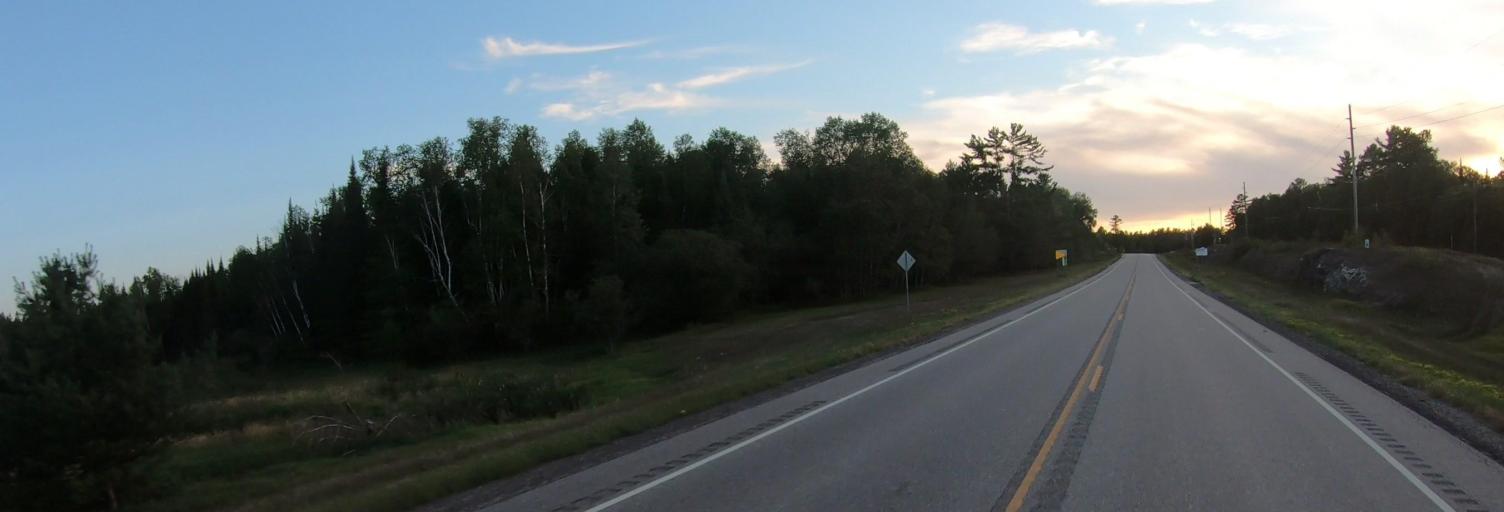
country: US
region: Minnesota
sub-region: Saint Louis County
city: Babbitt
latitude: 47.8539
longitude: -92.0522
